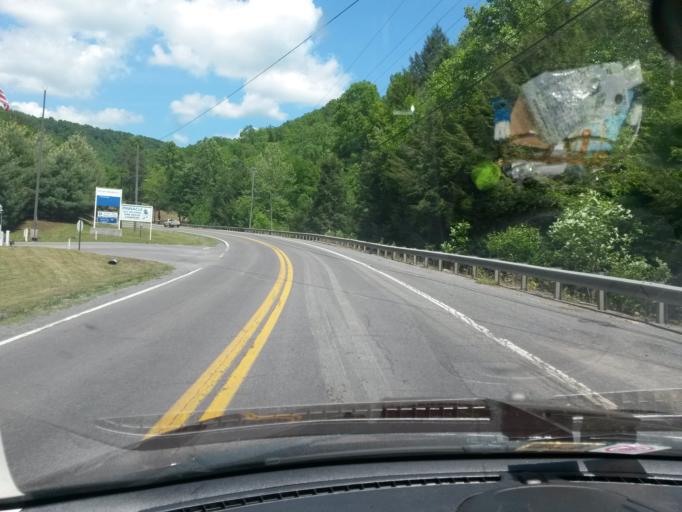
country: US
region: West Virginia
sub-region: Wyoming County
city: Pineville
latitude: 37.5015
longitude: -81.5374
